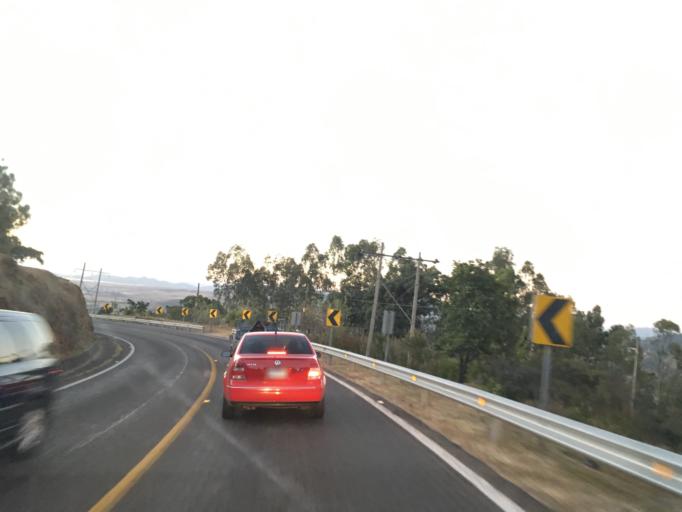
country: MX
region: Michoacan
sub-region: Zinapecuaro
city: Santa Clara del Tule
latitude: 19.8129
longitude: -100.8119
